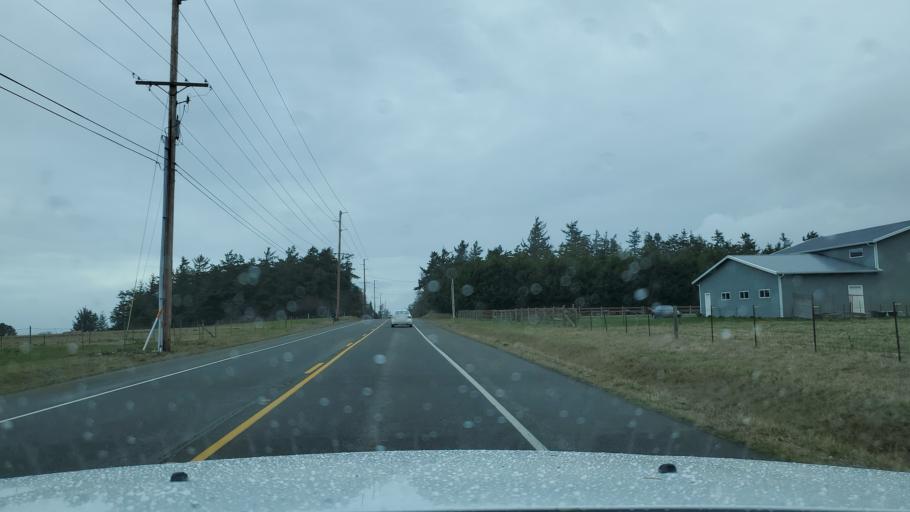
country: US
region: Washington
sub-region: Island County
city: Coupeville
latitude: 48.2500
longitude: -122.7516
